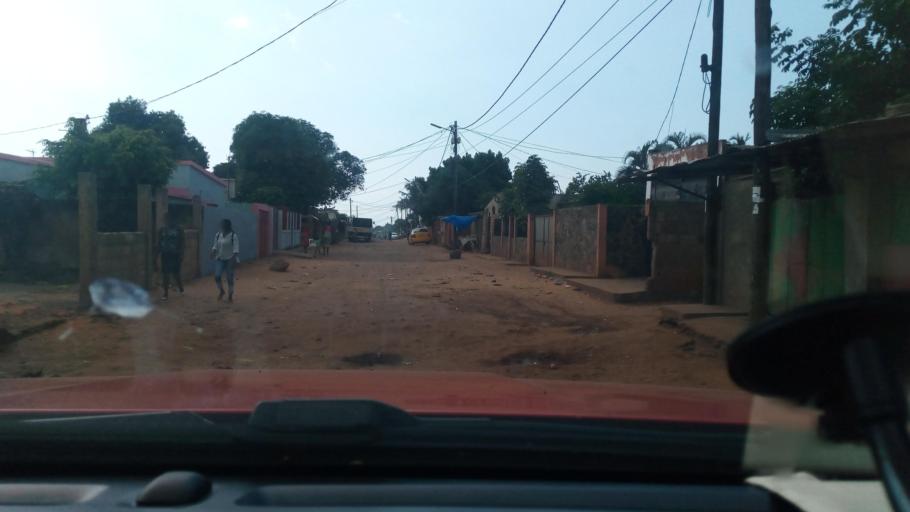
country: MZ
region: Maputo City
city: Maputo
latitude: -25.9199
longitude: 32.6002
